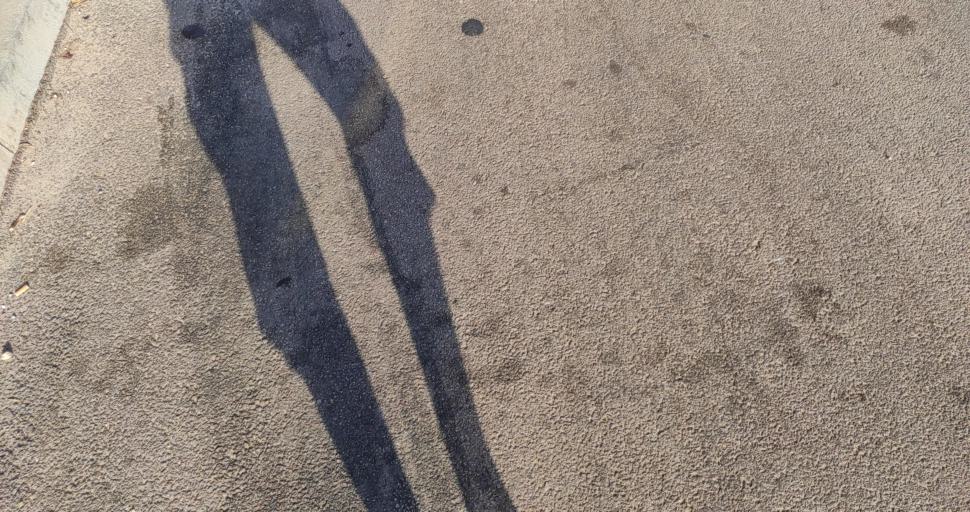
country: FR
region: Corsica
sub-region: Departement de la Corse-du-Sud
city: Alata
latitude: 41.9926
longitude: 8.6714
